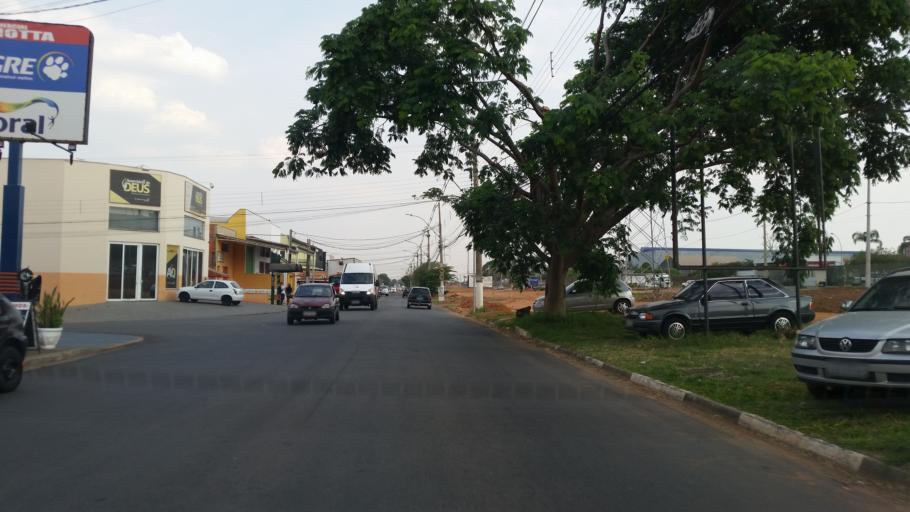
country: BR
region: Sao Paulo
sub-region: Hortolandia
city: Hortolandia
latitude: -22.8999
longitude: -47.1869
